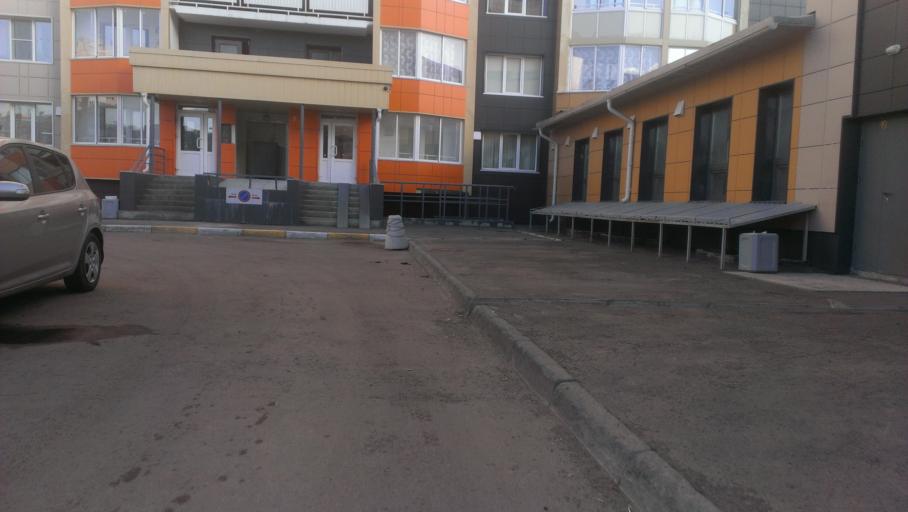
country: RU
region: Altai Krai
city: Novosilikatnyy
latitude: 53.3376
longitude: 83.6597
